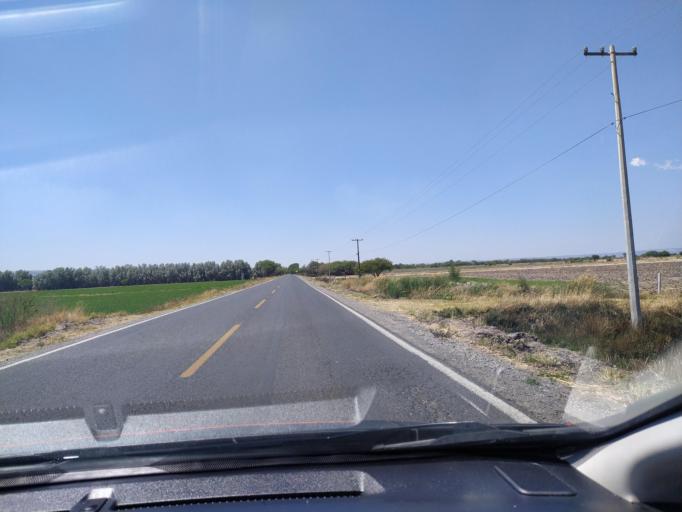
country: MX
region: Guanajuato
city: Ciudad Manuel Doblado
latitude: 20.7439
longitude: -101.8936
